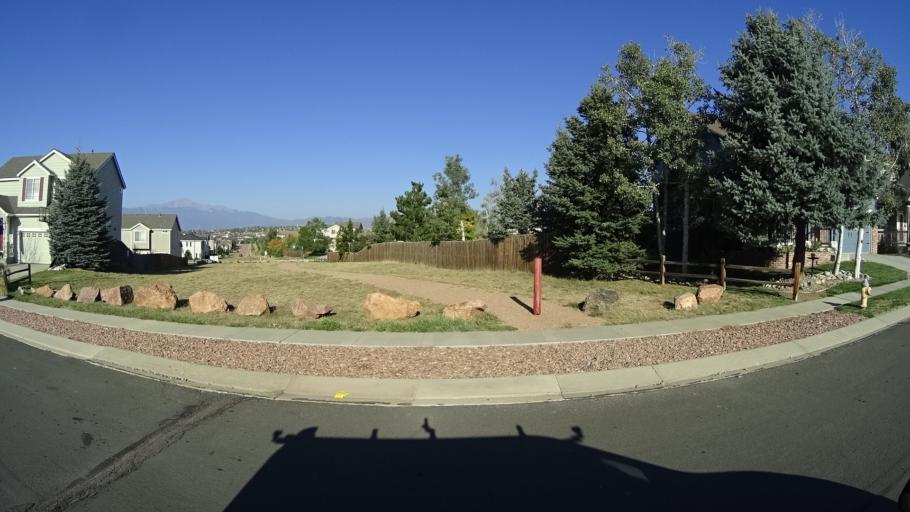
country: US
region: Colorado
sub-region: El Paso County
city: Cimarron Hills
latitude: 38.8882
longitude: -104.6946
